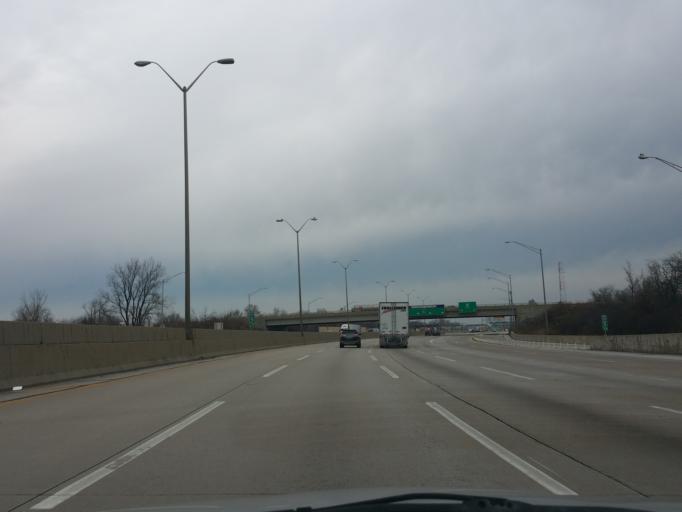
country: US
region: Illinois
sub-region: Cook County
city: University Park
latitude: 41.5841
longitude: -87.6806
